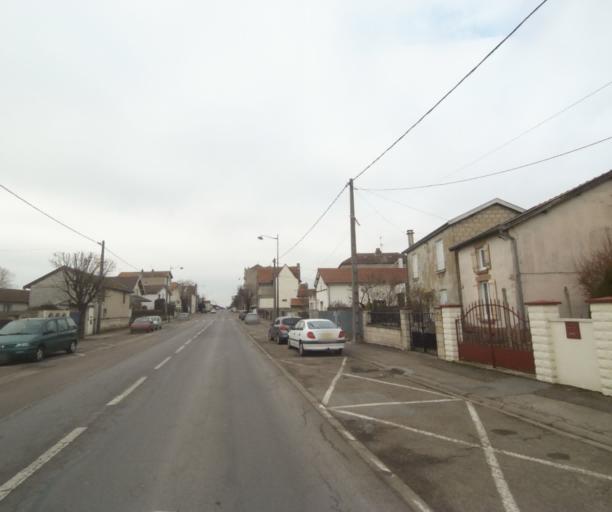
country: FR
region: Champagne-Ardenne
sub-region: Departement de la Haute-Marne
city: Bettancourt-la-Ferree
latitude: 48.6360
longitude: 4.9679
